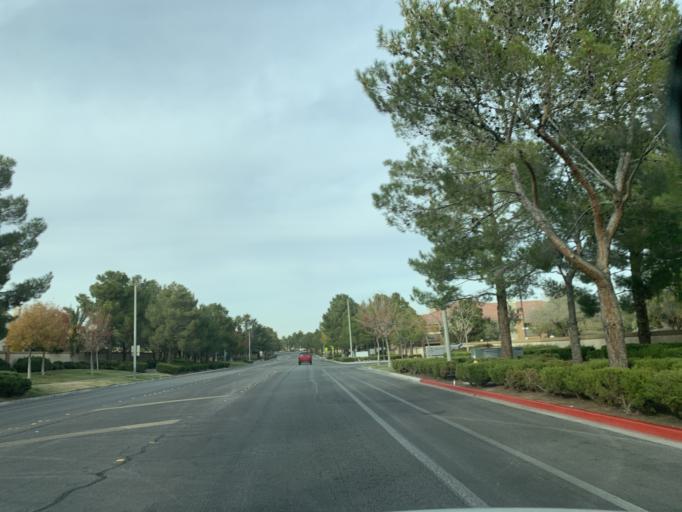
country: US
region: Nevada
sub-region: Clark County
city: Summerlin South
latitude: 36.1454
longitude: -115.3067
